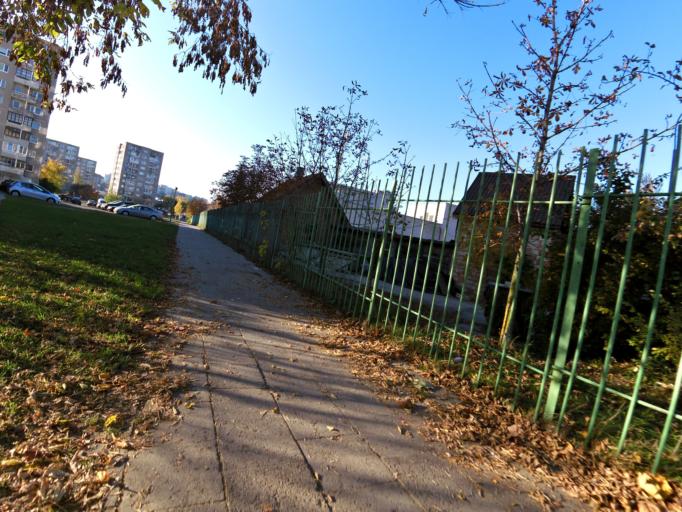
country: LT
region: Vilnius County
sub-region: Vilnius
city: Fabijoniskes
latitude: 54.7359
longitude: 25.2396
